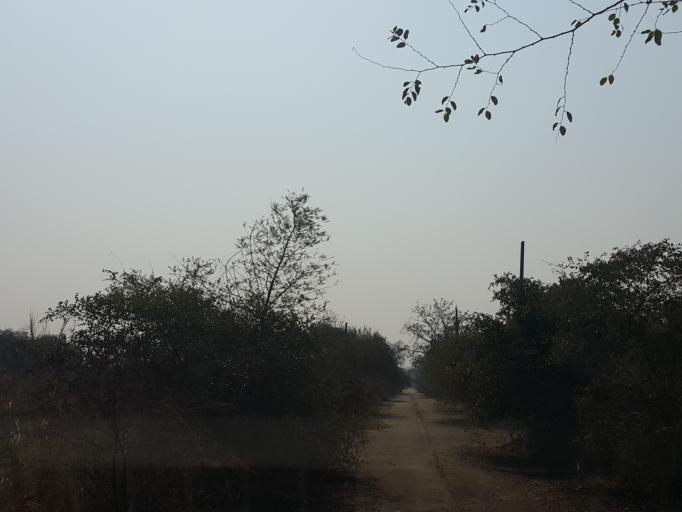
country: TH
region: Chiang Mai
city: San Kamphaeng
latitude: 18.7831
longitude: 99.0737
